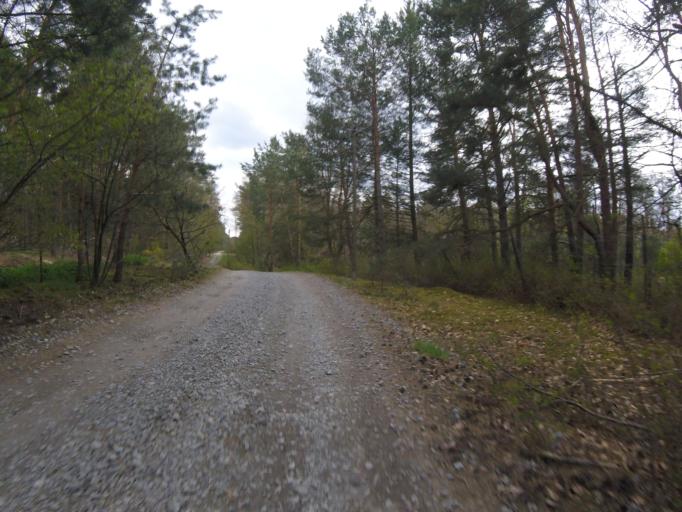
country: DE
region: Brandenburg
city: Schwerin
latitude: 52.1706
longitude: 13.6383
